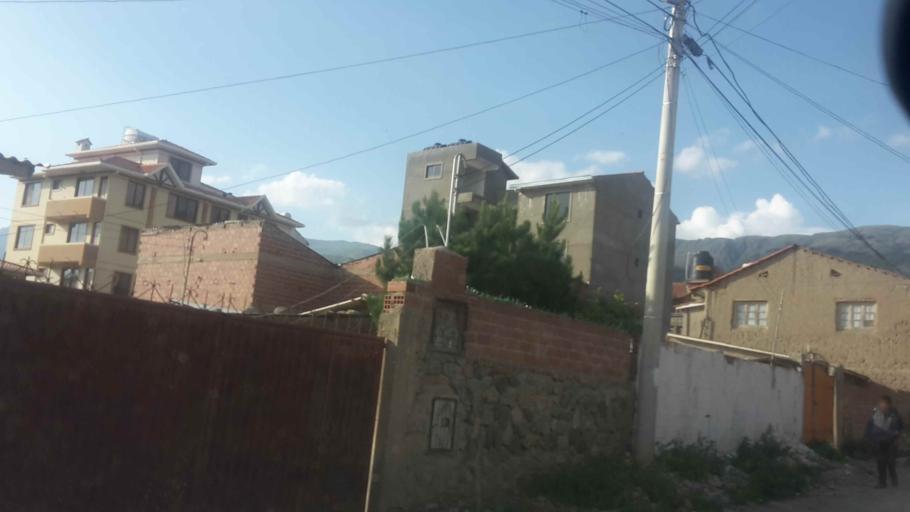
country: BO
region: Cochabamba
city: Cochabamba
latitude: -17.3406
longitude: -66.2204
